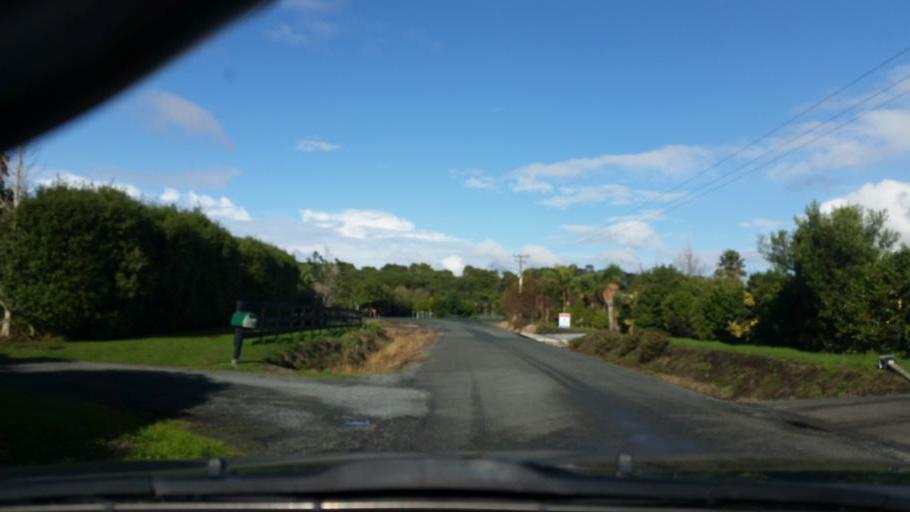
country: NZ
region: Auckland
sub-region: Auckland
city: Wellsford
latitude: -36.0943
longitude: 174.5747
